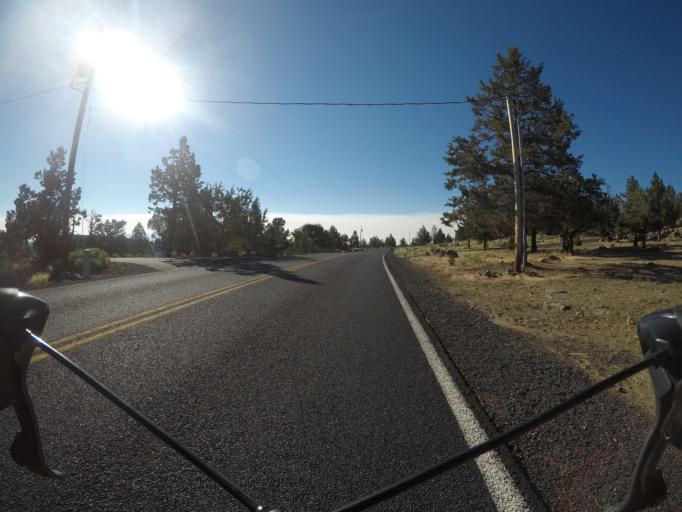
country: US
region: Oregon
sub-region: Deschutes County
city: Redmond
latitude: 44.1817
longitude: -121.2680
